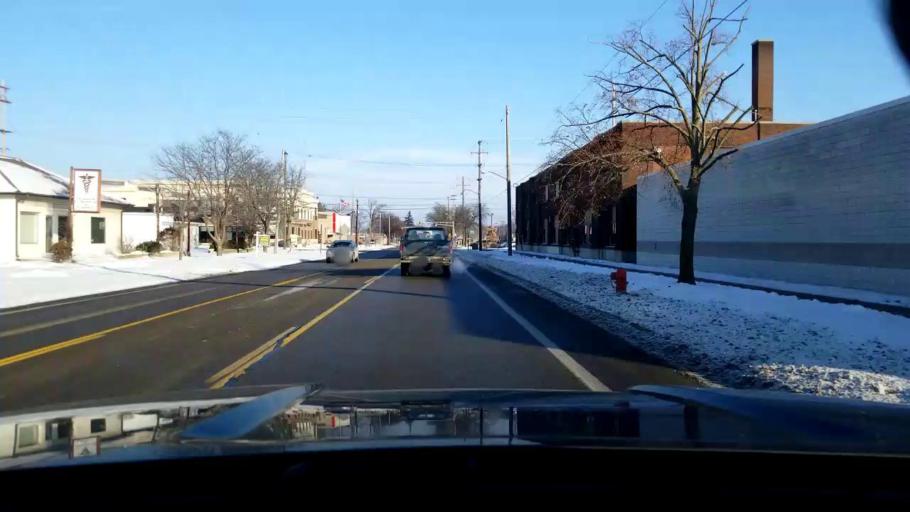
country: US
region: Michigan
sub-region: Jackson County
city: Jackson
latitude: 42.2513
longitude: -84.4088
